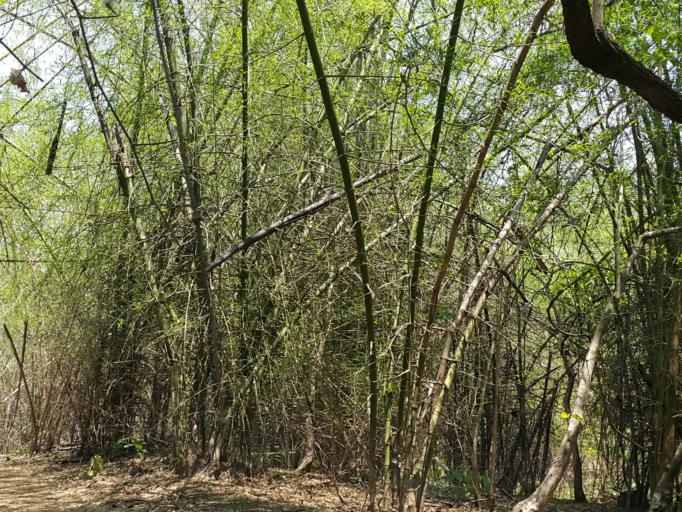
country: TH
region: Kanchanaburi
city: Sai Yok
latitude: 14.2125
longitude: 98.8791
